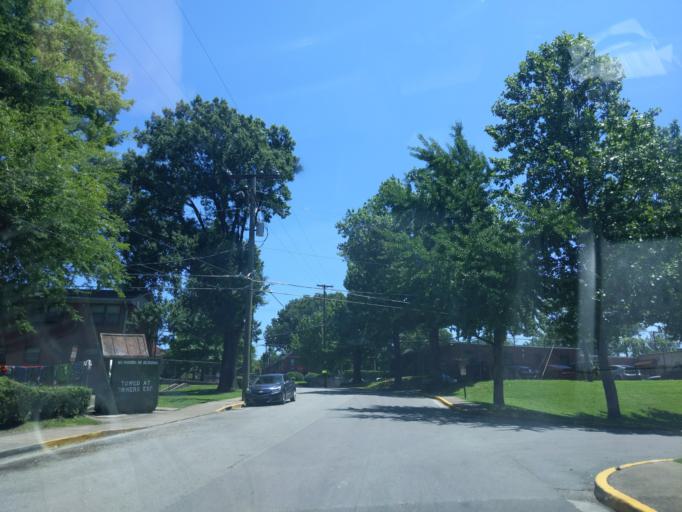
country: US
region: Tennessee
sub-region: Davidson County
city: Nashville
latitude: 36.1655
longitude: -86.7598
